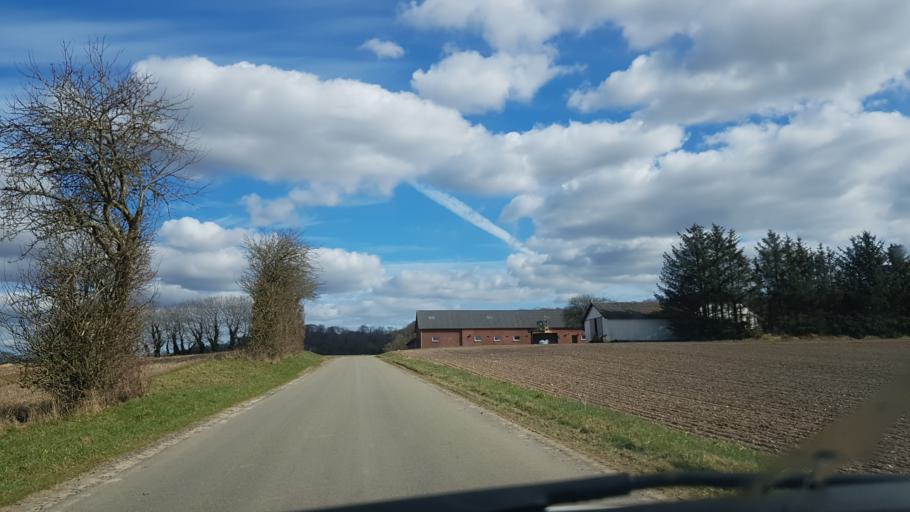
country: DK
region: South Denmark
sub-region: Kolding Kommune
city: Vamdrup
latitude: 55.3565
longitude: 9.3718
